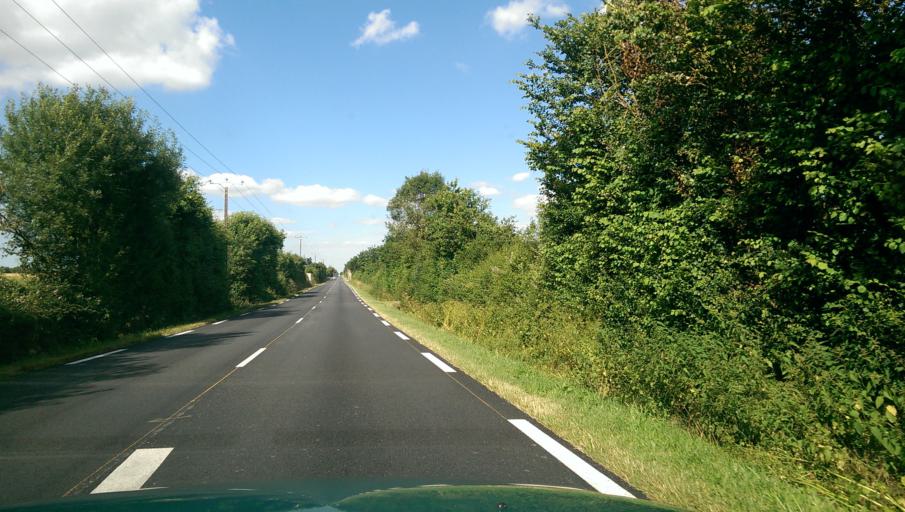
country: FR
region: Pays de la Loire
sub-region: Departement de la Loire-Atlantique
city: Lege
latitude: 46.8971
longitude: -1.5767
